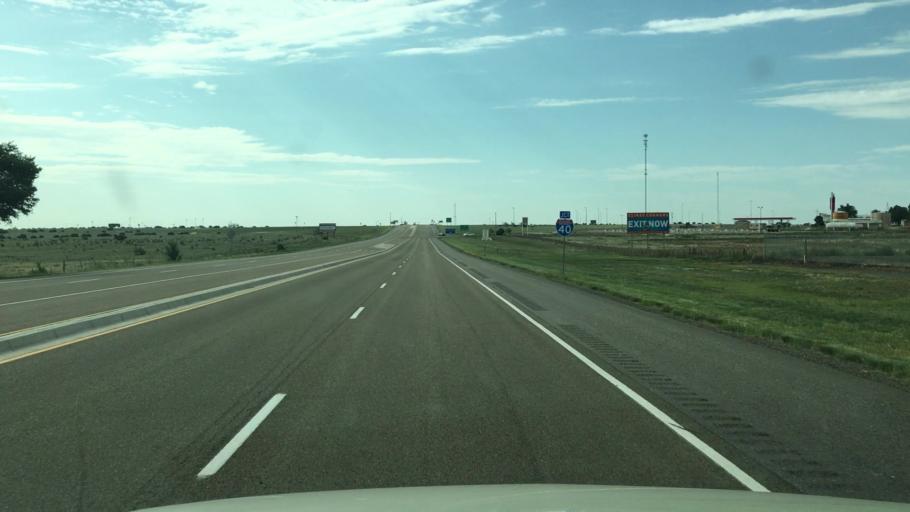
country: US
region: New Mexico
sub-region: Torrance County
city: Moriarty
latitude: 35.0153
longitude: -105.6682
